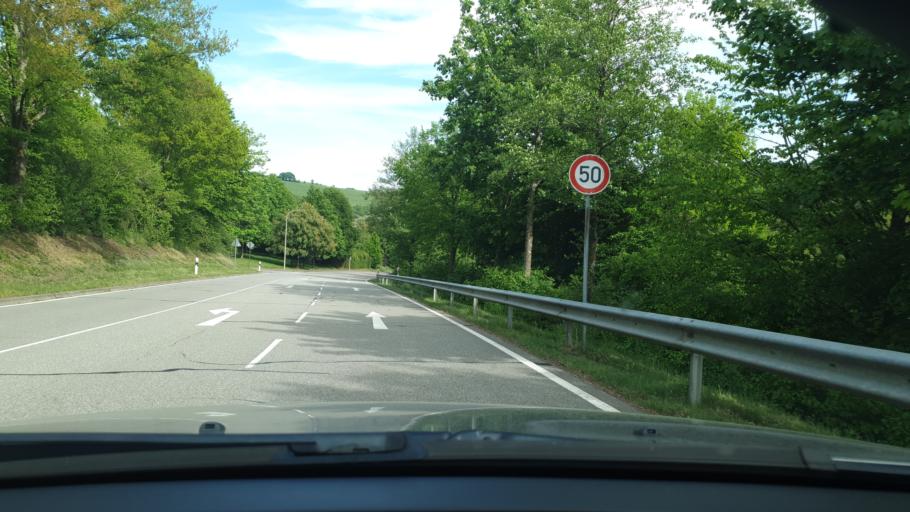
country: DE
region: Rheinland-Pfalz
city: Schmitshausen
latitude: 49.3177
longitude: 7.5127
